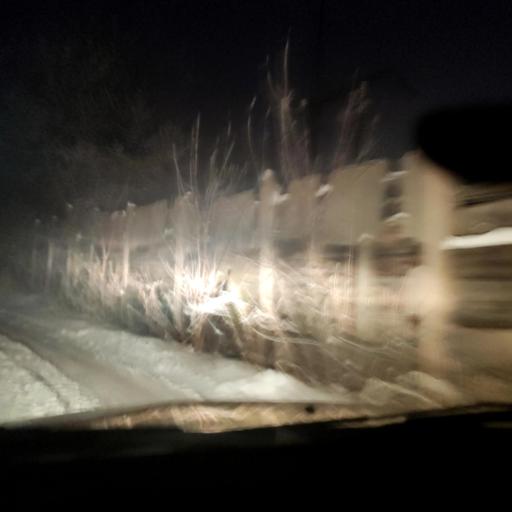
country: RU
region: Bashkortostan
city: Ufa
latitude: 54.7986
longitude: 56.0341
